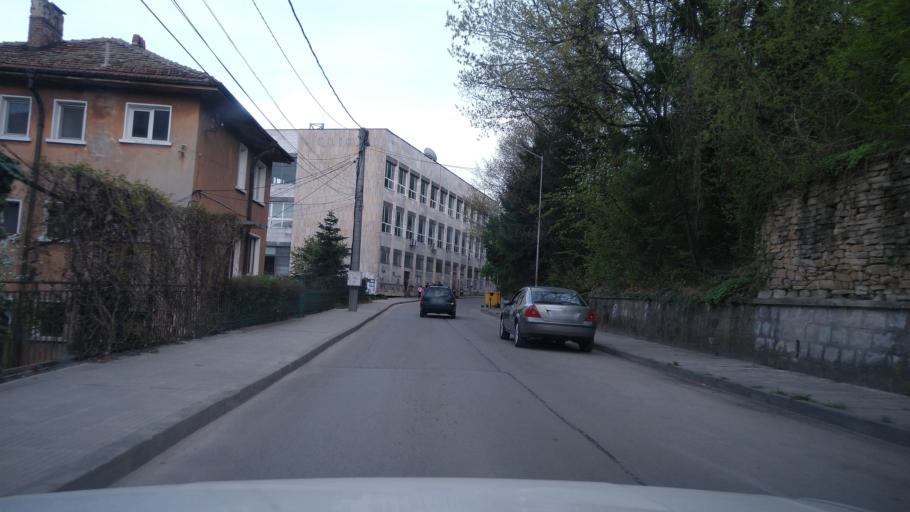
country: BG
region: Gabrovo
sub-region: Obshtina Gabrovo
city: Gabrovo
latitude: 42.8667
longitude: 25.3163
